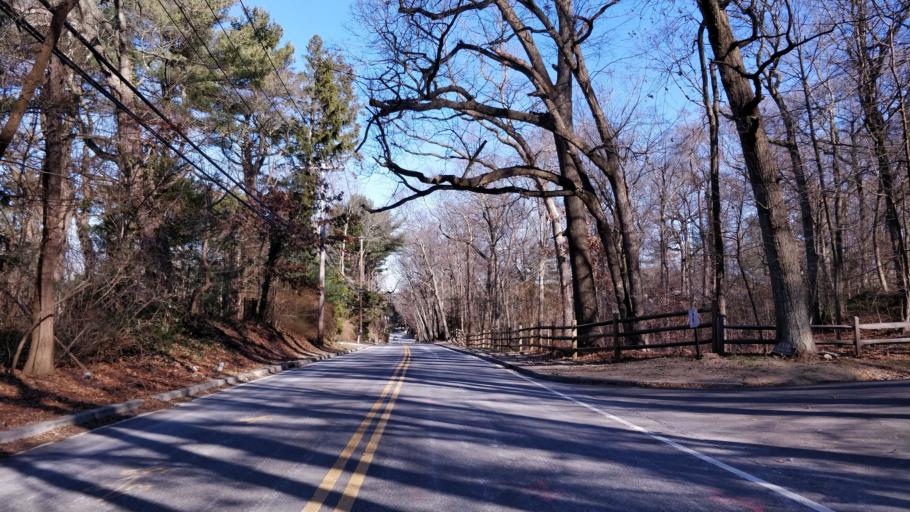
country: US
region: New York
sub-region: Nassau County
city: Brookville
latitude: 40.8136
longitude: -73.5764
